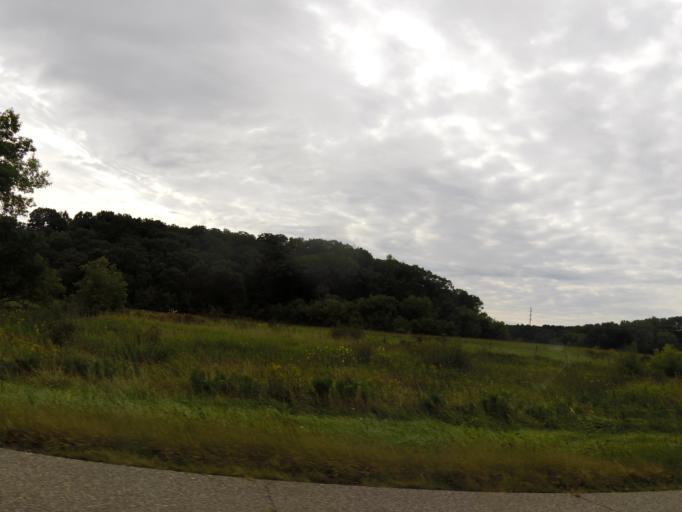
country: US
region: Wisconsin
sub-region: Monroe County
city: Tomah
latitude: 43.9458
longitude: -90.5645
